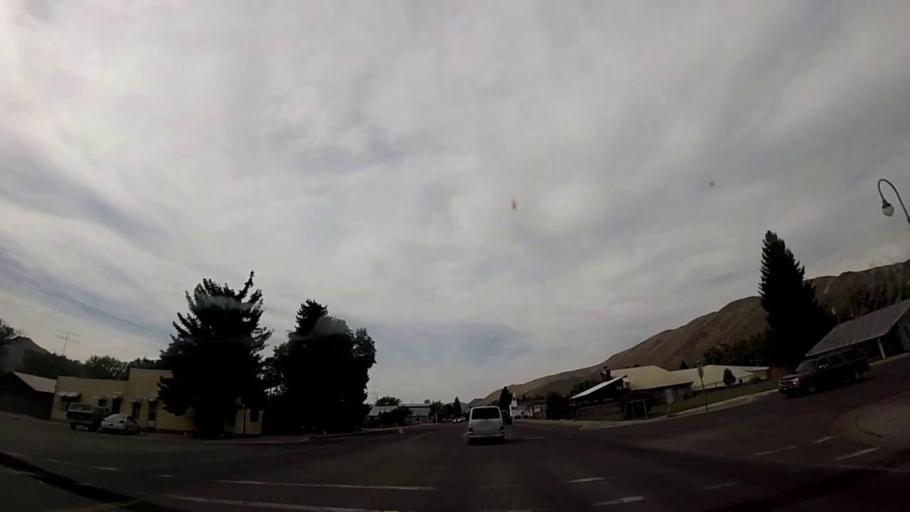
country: US
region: Idaho
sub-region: Blaine County
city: Bellevue
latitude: 43.4646
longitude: -114.2609
